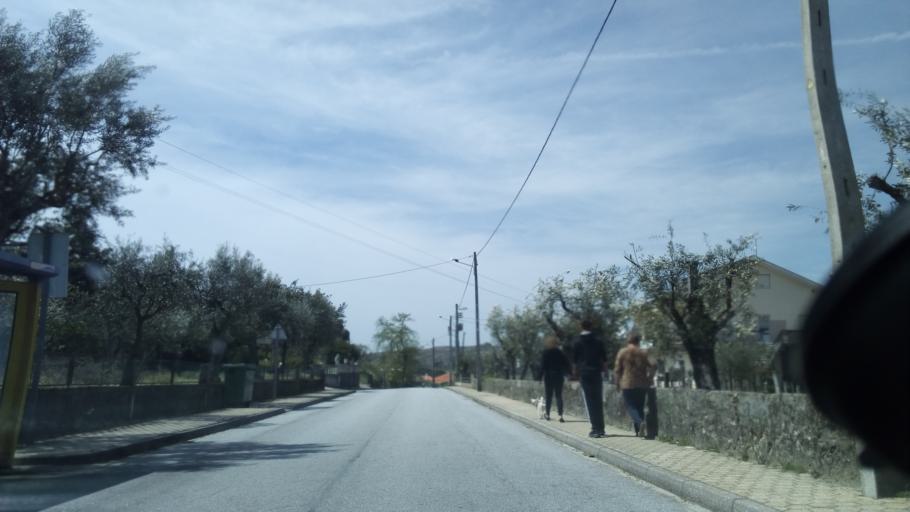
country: PT
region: Viseu
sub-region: Mangualde
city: Mangualde
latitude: 40.6111
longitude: -7.7825
